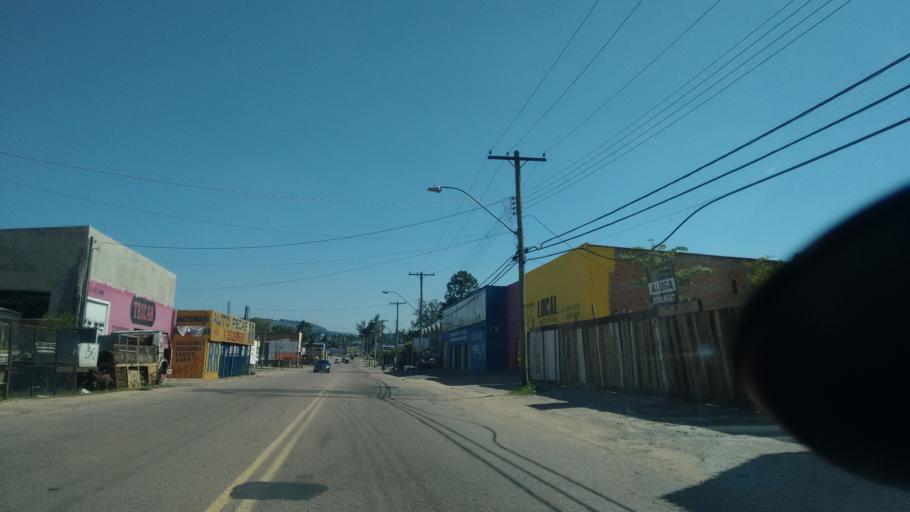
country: BR
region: Rio Grande do Sul
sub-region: Cachoeirinha
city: Cachoeirinha
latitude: -30.0078
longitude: -51.1280
